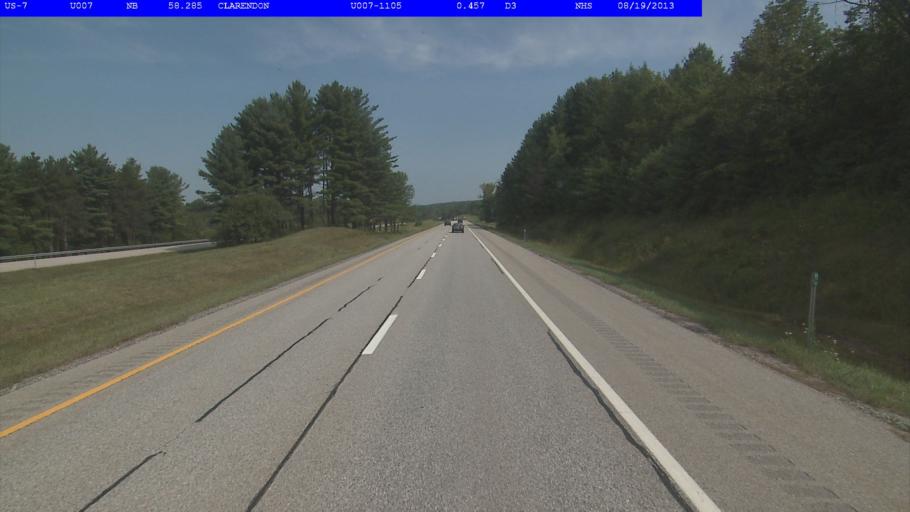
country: US
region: Vermont
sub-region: Rutland County
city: Rutland
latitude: 43.5006
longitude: -72.9678
